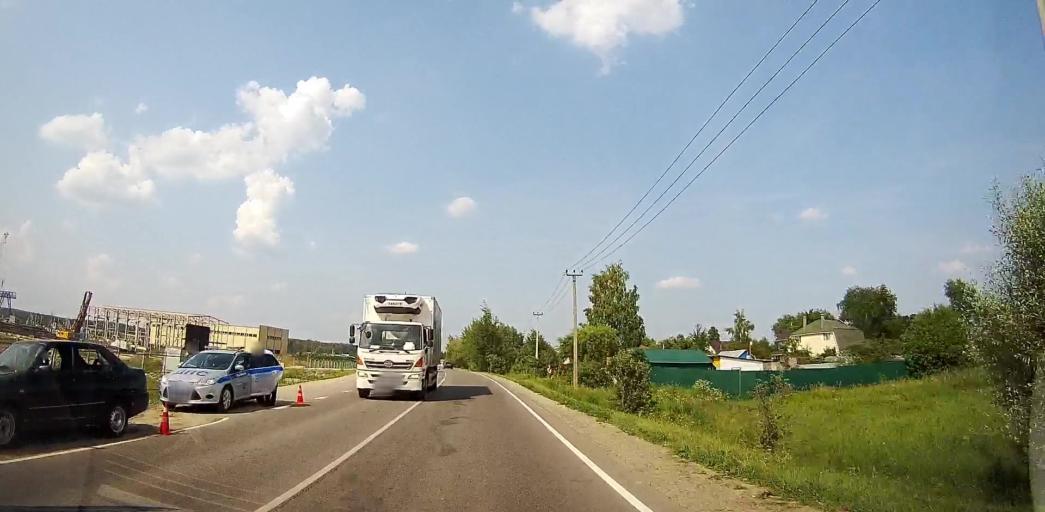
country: RU
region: Moskovskaya
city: Mikhnevo
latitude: 55.1561
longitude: 37.9600
